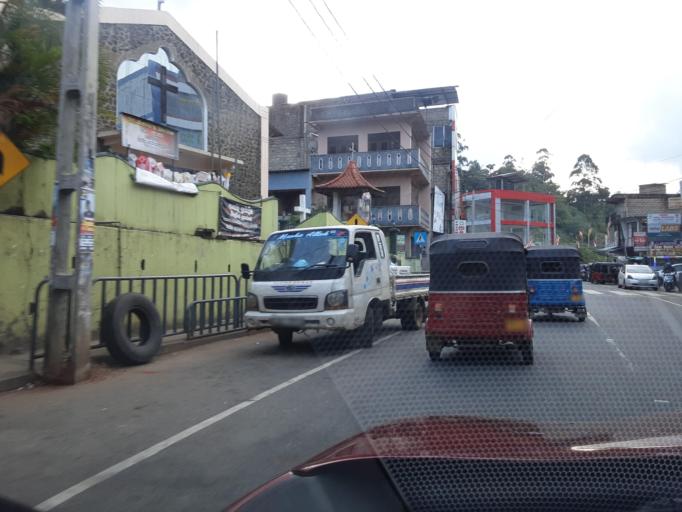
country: LK
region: Central
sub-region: Nuwara Eliya District
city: Nuwara Eliya
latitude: 6.9056
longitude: 80.9104
